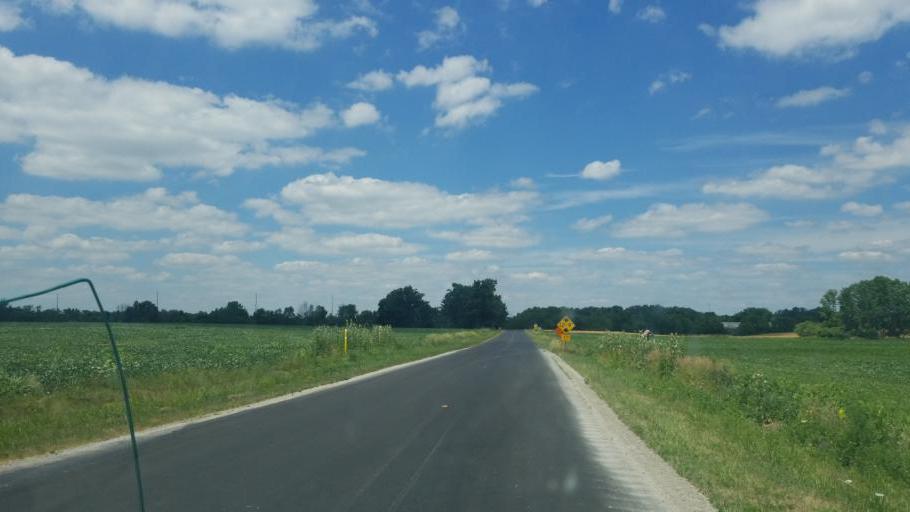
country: US
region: Ohio
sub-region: Williams County
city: Edgerton
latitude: 41.4495
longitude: -84.7103
